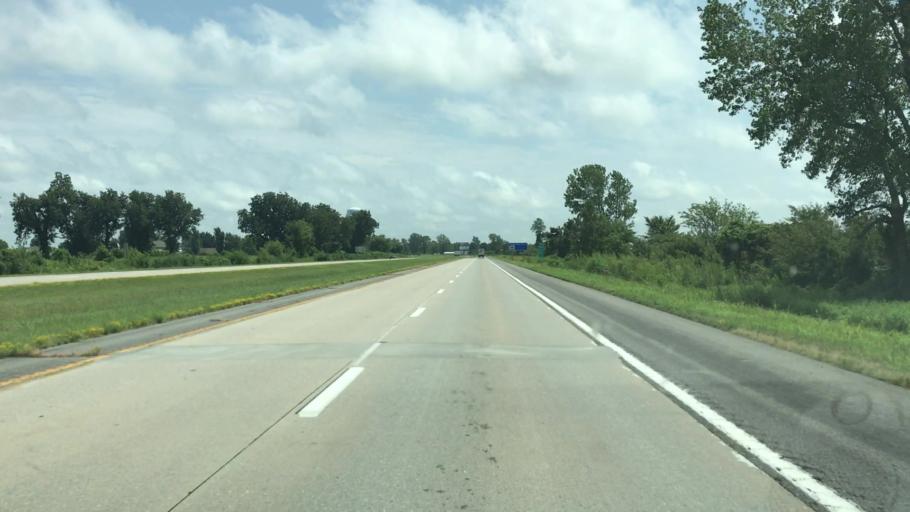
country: US
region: Missouri
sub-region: Pemiscot County
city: Caruthersville
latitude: 36.1610
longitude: -89.6783
